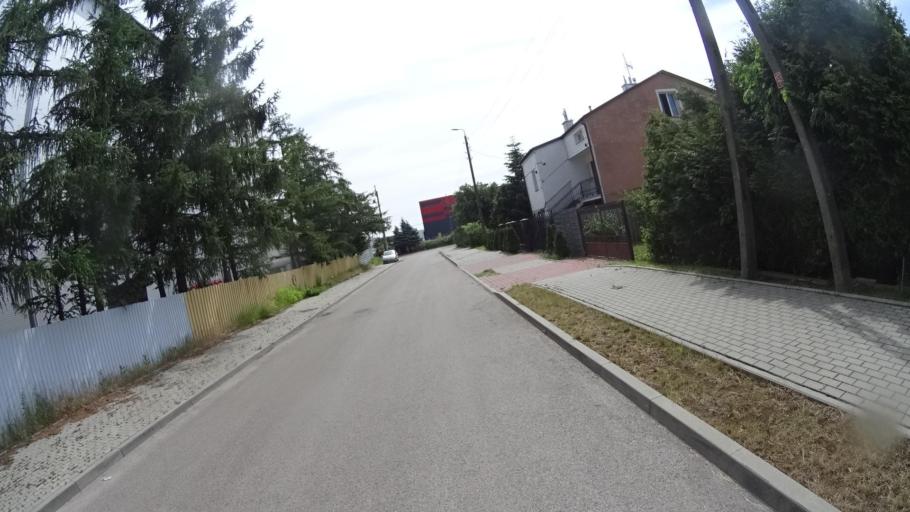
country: PL
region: Masovian Voivodeship
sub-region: Warszawa
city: Wlochy
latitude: 52.1794
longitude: 20.9288
